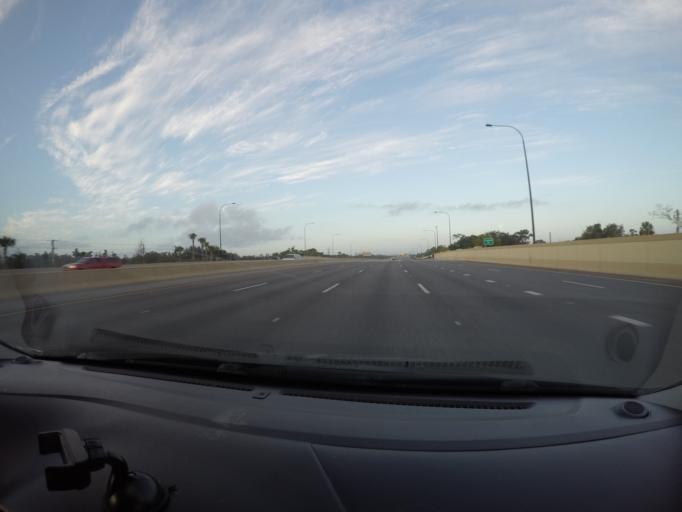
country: US
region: Florida
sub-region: Orange County
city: Azalea Park
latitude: 28.5398
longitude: -81.2907
